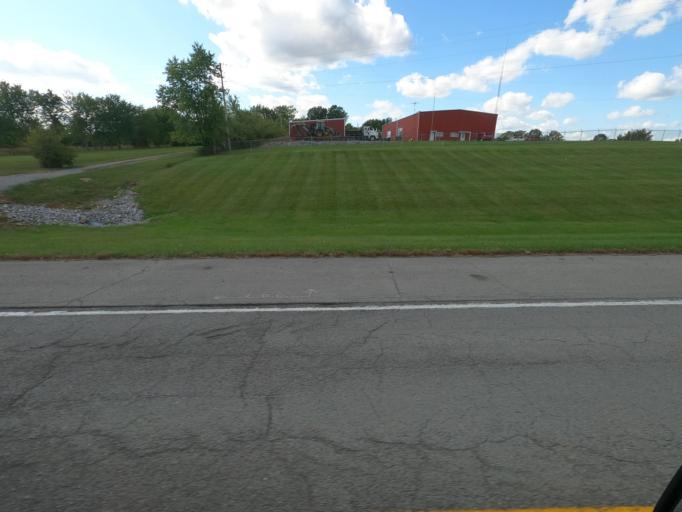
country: US
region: Illinois
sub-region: Johnson County
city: Vienna
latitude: 37.4329
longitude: -88.8928
